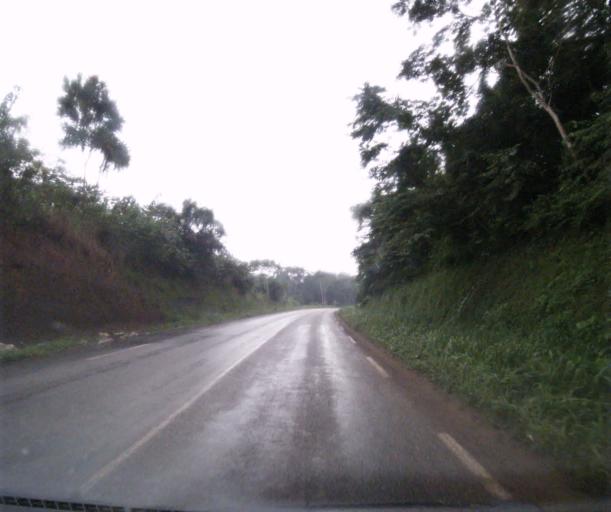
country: CM
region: Centre
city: Eseka
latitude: 3.8709
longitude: 10.6353
